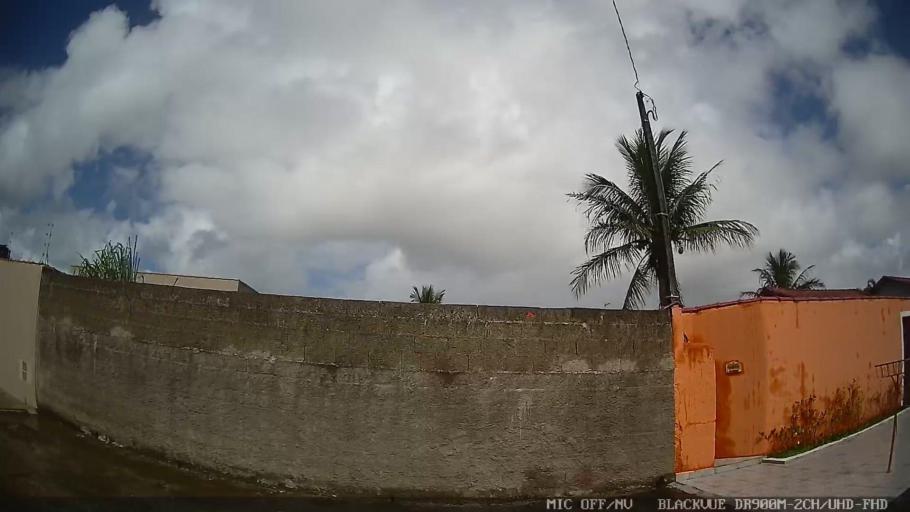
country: BR
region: Sao Paulo
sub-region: Itanhaem
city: Itanhaem
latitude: -24.2291
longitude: -46.8764
